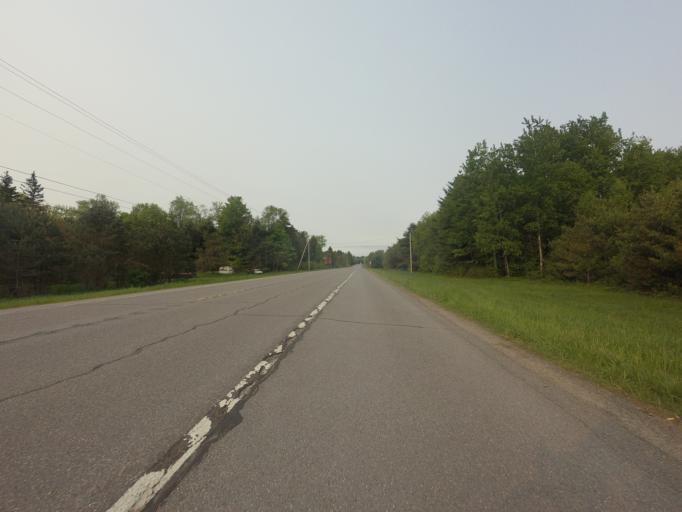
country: US
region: New York
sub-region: Jefferson County
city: Carthage
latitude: 44.0832
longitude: -75.4353
